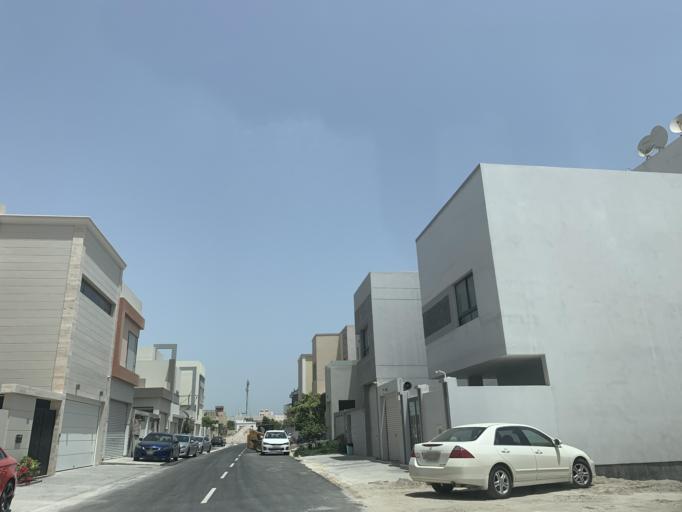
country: BH
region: Northern
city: Madinat `Isa
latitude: 26.1601
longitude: 50.5795
